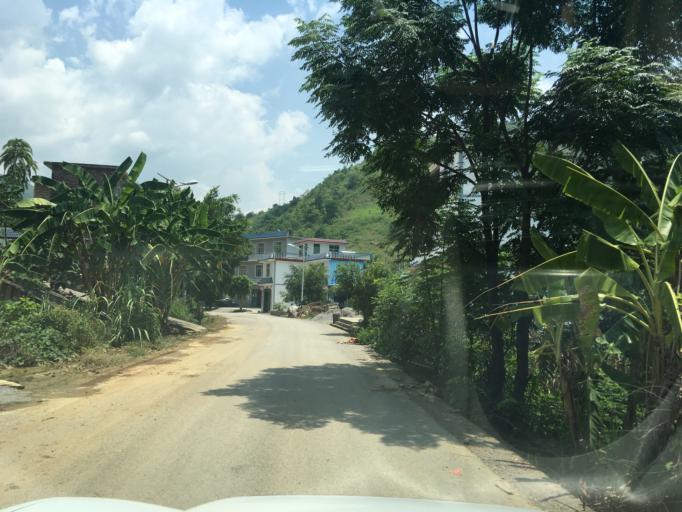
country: CN
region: Guangxi Zhuangzu Zizhiqu
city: Xinzhou
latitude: 24.9064
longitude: 105.4724
